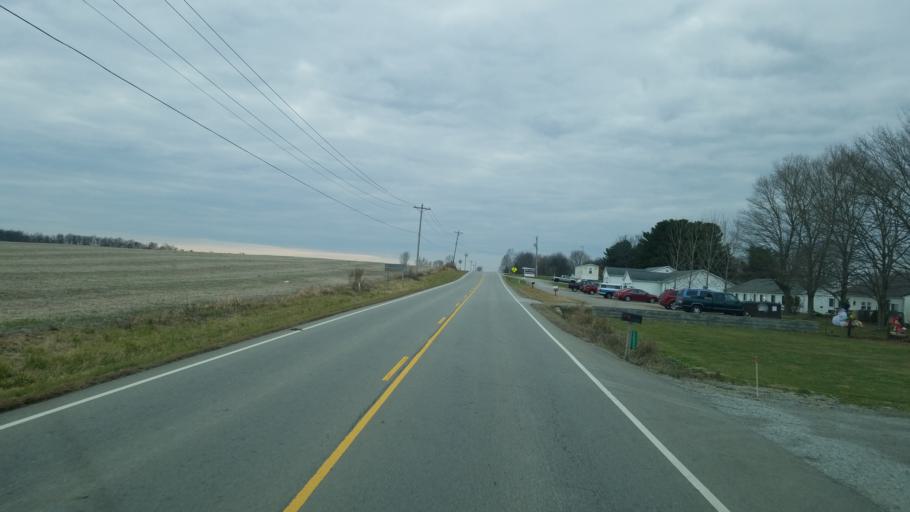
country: US
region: Ohio
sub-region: Highland County
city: Greenfield
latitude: 39.2173
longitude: -83.4416
